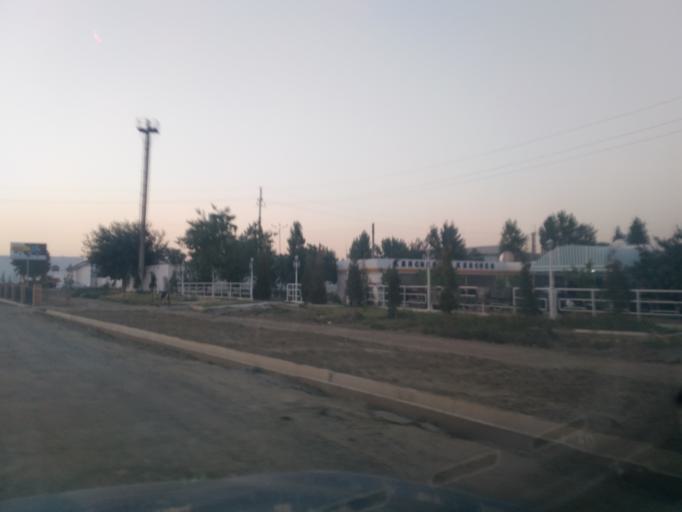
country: UZ
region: Sirdaryo
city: Guliston
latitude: 40.5053
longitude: 68.7682
